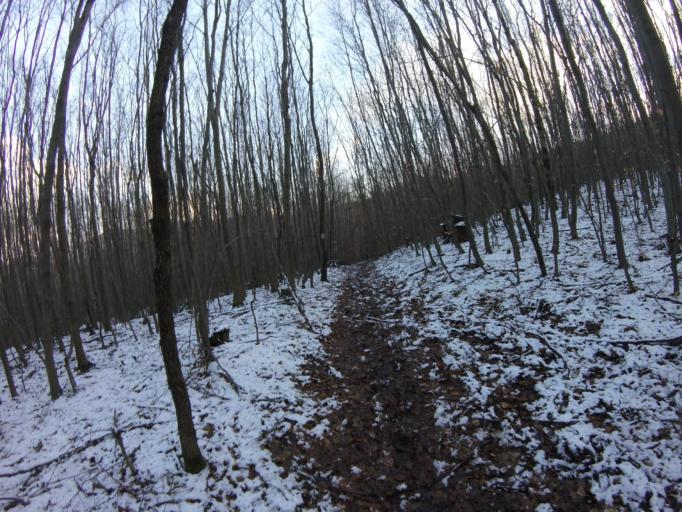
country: HU
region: Pest
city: Pilisszentkereszt
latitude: 47.7352
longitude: 18.8890
